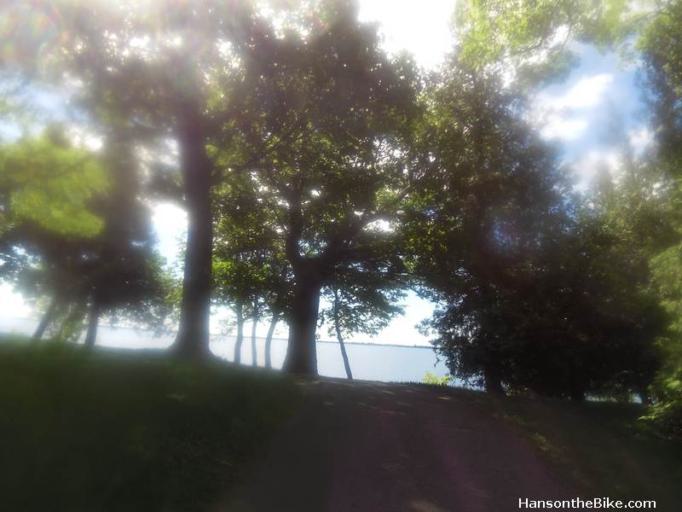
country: CA
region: Ontario
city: Kingston
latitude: 44.2143
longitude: -76.5252
